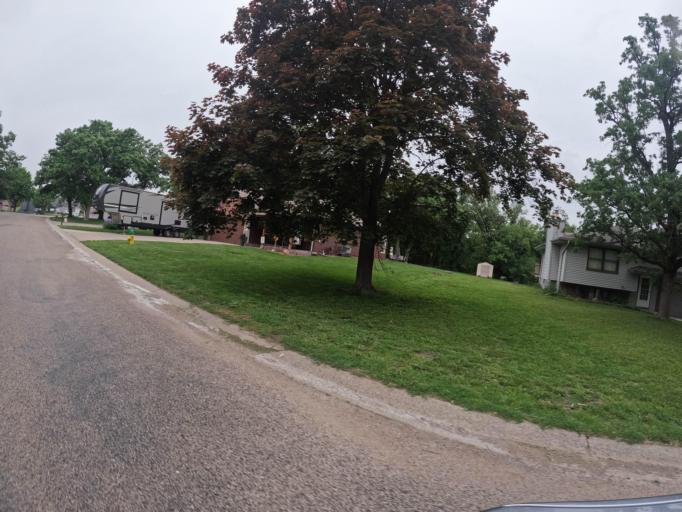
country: US
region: Nebraska
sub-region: Sarpy County
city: Offutt Air Force Base
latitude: 41.0488
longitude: -95.9703
